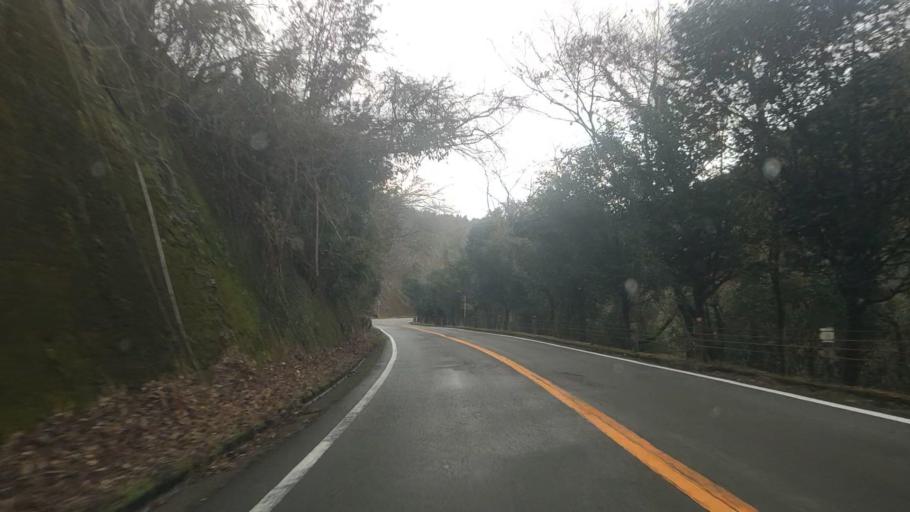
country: JP
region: Kumamoto
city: Hitoyoshi
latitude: 32.1257
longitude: 130.8130
